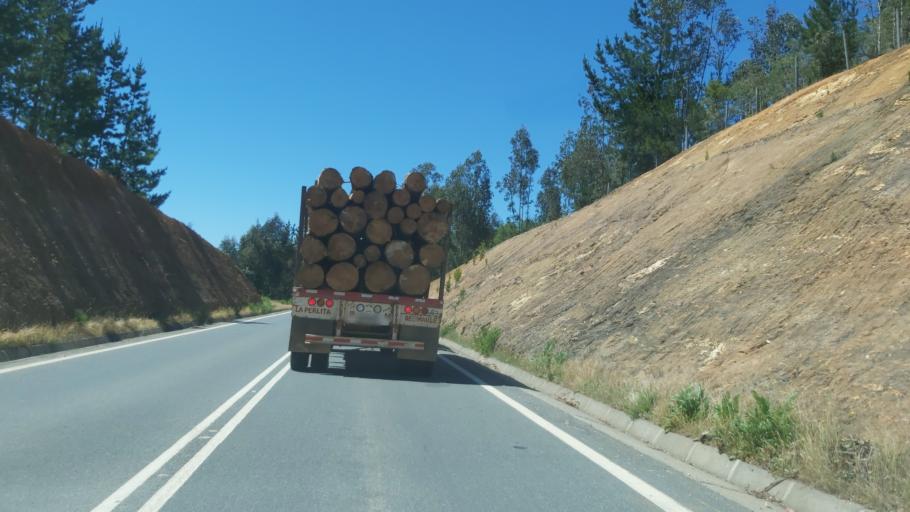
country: CL
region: Maule
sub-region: Provincia de Talca
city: Constitucion
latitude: -34.9376
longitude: -71.9810
